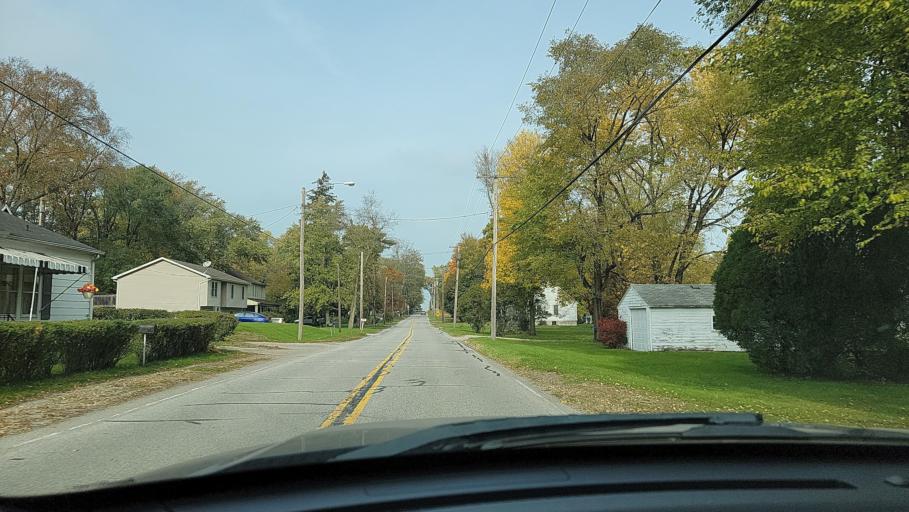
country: US
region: Indiana
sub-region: Porter County
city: Portage
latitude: 41.5879
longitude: -87.1736
